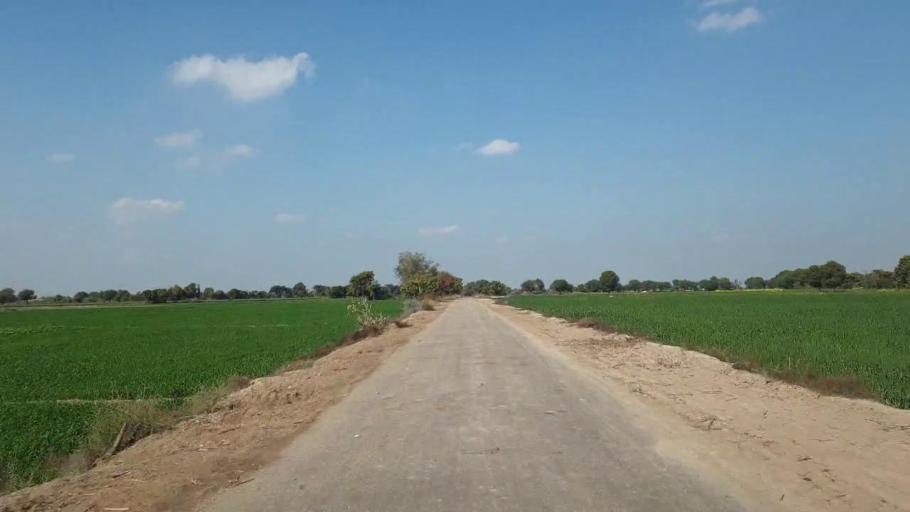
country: PK
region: Sindh
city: Shahpur Chakar
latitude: 26.0739
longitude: 68.5839
